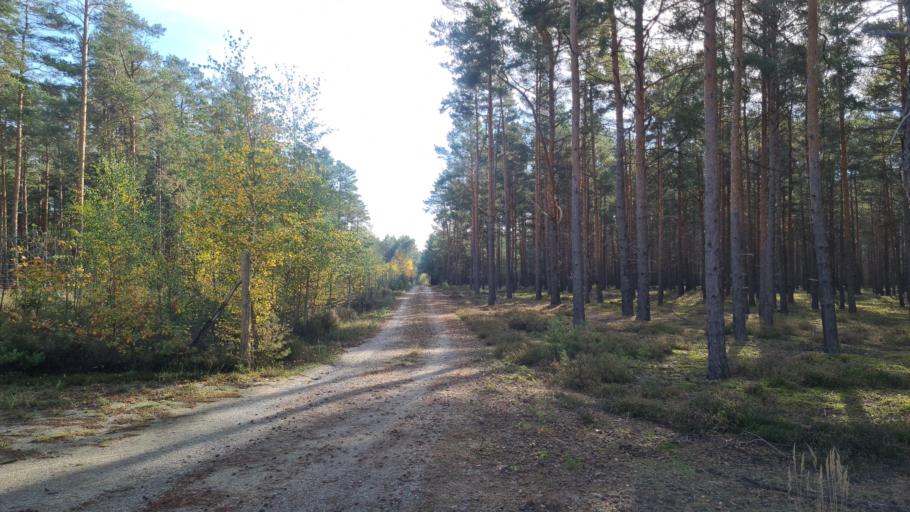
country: DE
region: Brandenburg
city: Sallgast
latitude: 51.6365
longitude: 13.8330
